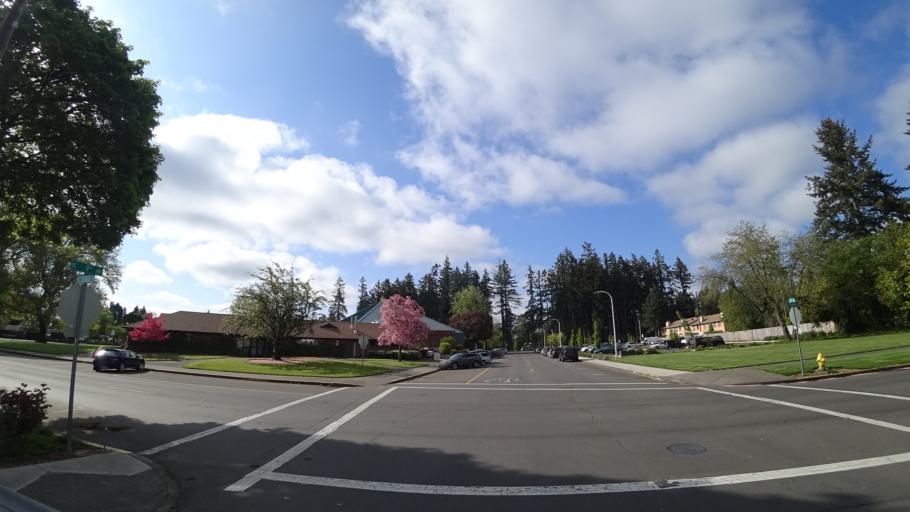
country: US
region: Oregon
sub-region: Washington County
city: Hillsboro
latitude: 45.5163
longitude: -122.9756
